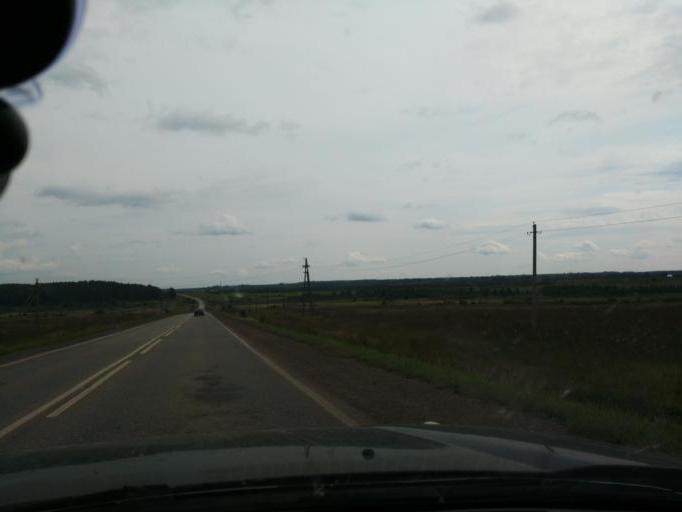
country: RU
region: Perm
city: Kuyeda
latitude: 56.4697
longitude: 55.7096
